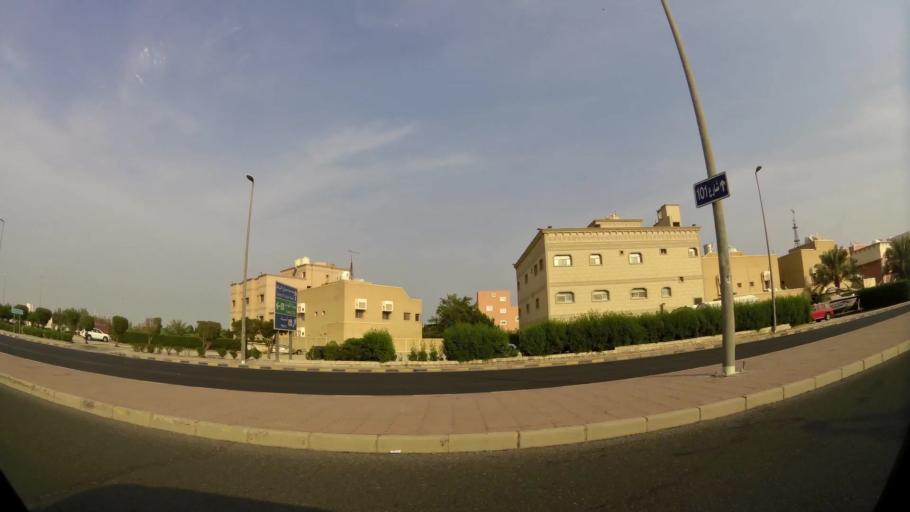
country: KW
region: Mubarak al Kabir
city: Sabah as Salim
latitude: 29.2401
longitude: 48.0612
